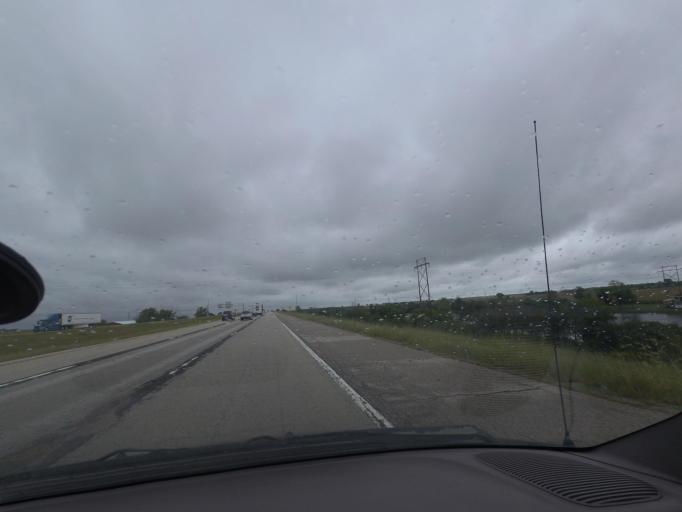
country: US
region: Illinois
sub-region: Macon County
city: Harristown
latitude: 39.8485
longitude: -89.0456
